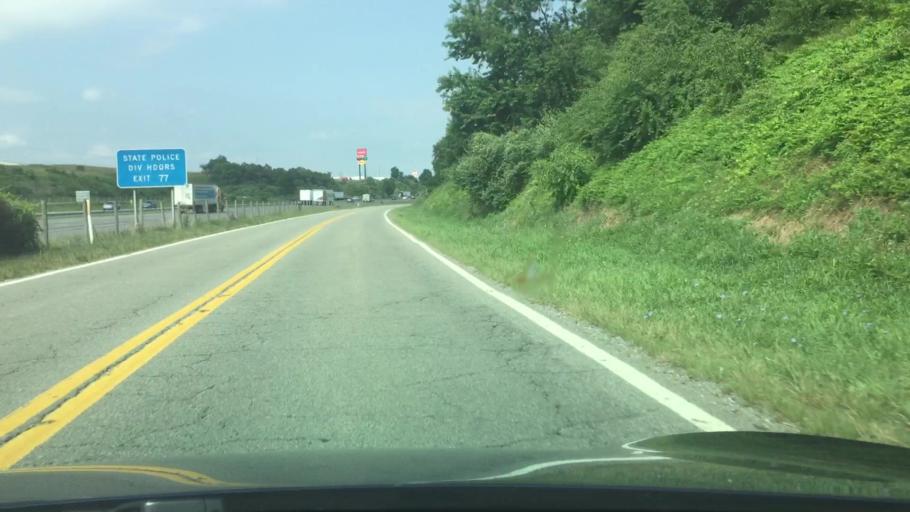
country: US
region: Virginia
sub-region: Wythe County
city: Wytheville
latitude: 36.9381
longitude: -80.9852
